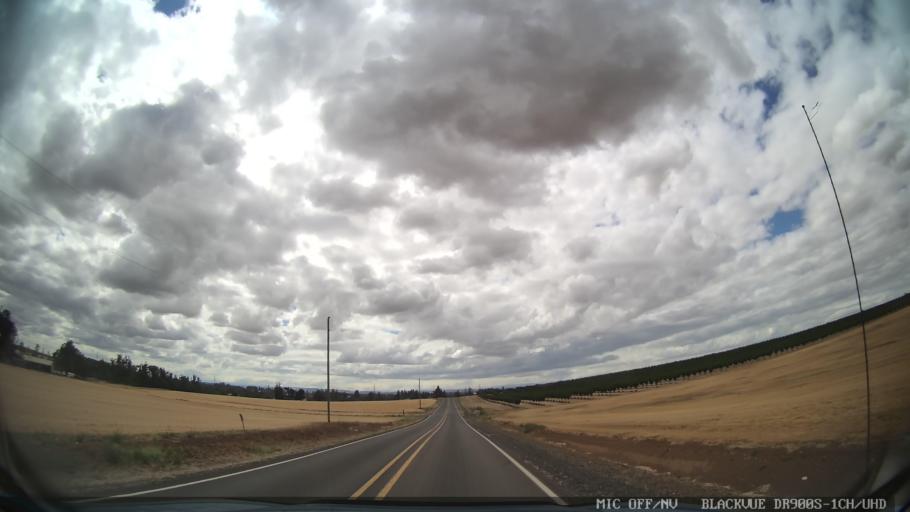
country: US
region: Oregon
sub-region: Marion County
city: Sublimity
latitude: 44.8443
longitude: -122.7560
